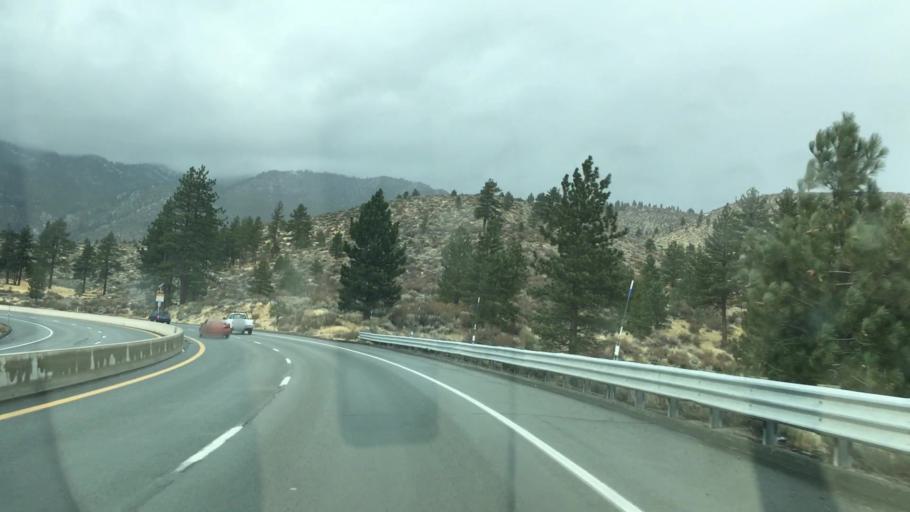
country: US
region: Nevada
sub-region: Douglas County
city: Indian Hills
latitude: 39.1205
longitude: -119.8169
